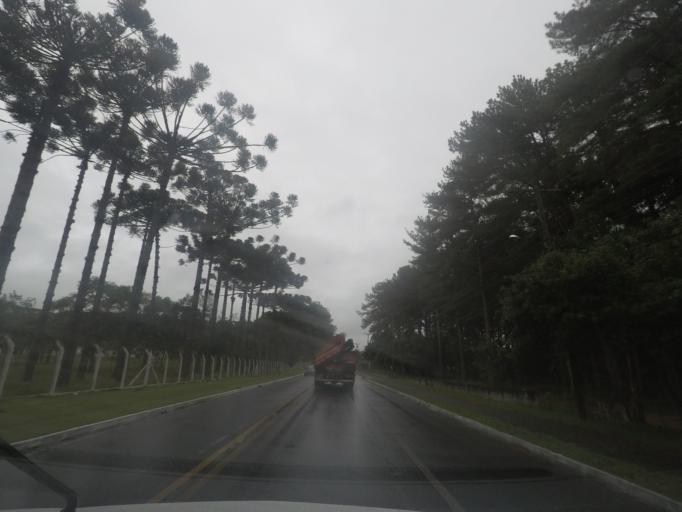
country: BR
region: Parana
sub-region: Quatro Barras
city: Quatro Barras
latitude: -25.3811
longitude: -49.1257
